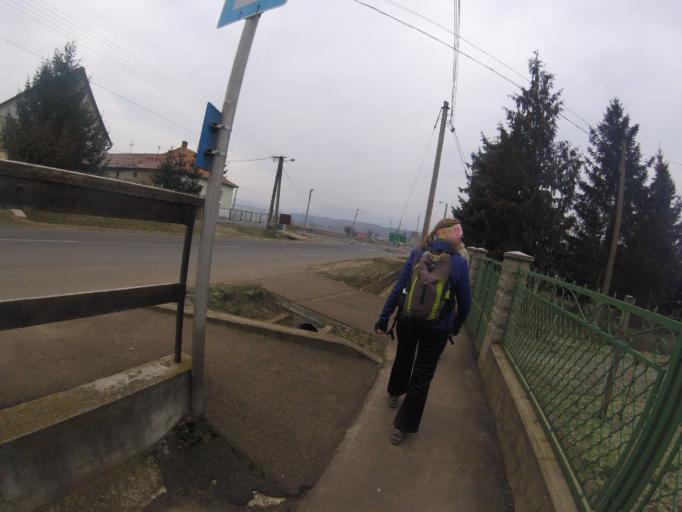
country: HU
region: Nograd
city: Paszto
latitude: 47.9451
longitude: 19.7015
